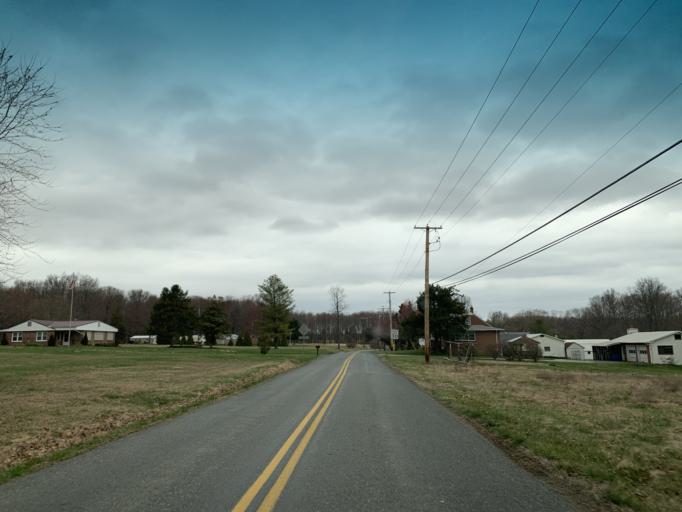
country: US
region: Maryland
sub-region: Harford County
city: Aberdeen
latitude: 39.5543
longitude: -76.1959
